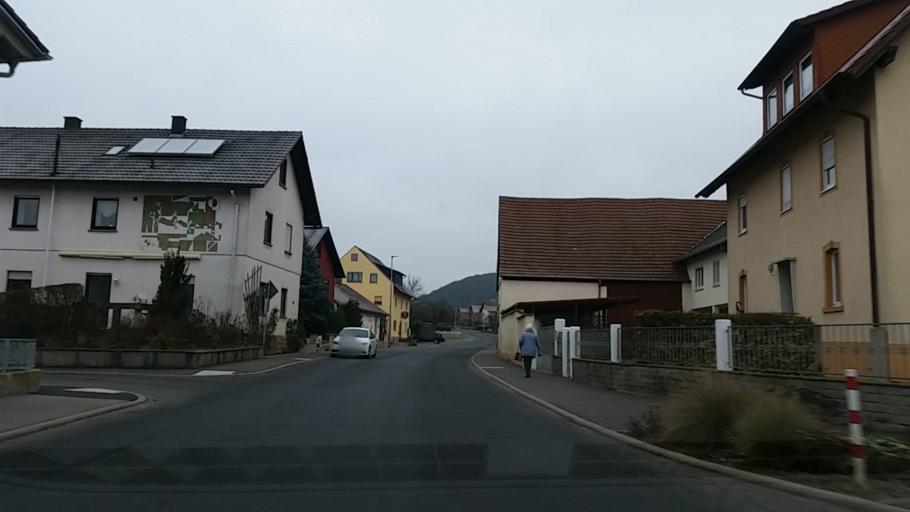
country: DE
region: Bavaria
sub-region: Regierungsbezirk Unterfranken
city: Fuchsstadt
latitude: 50.1092
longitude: 9.9323
